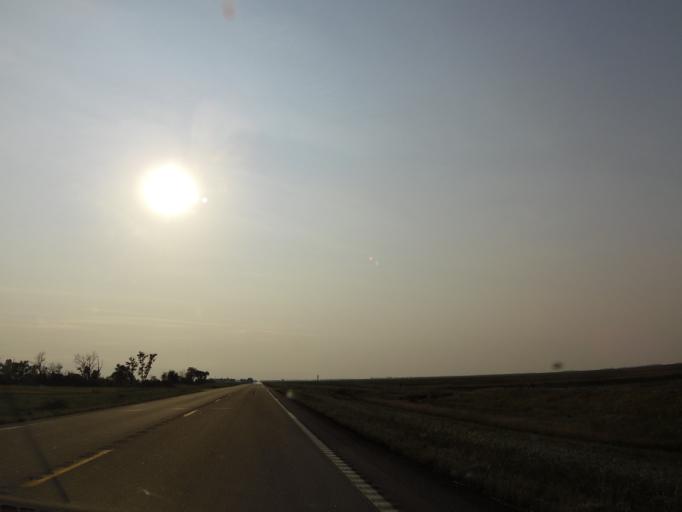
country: US
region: North Dakota
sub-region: Traill County
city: Hillsboro
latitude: 47.3529
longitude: -97.1751
